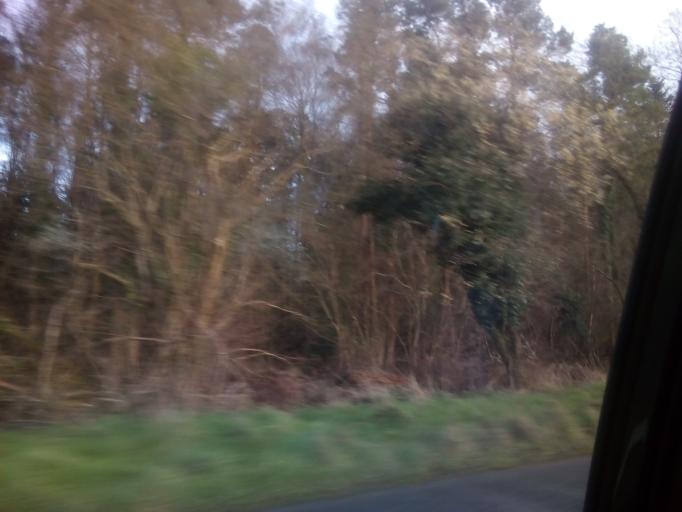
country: IE
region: Leinster
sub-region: Laois
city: Abbeyleix
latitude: 52.9029
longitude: -7.3557
